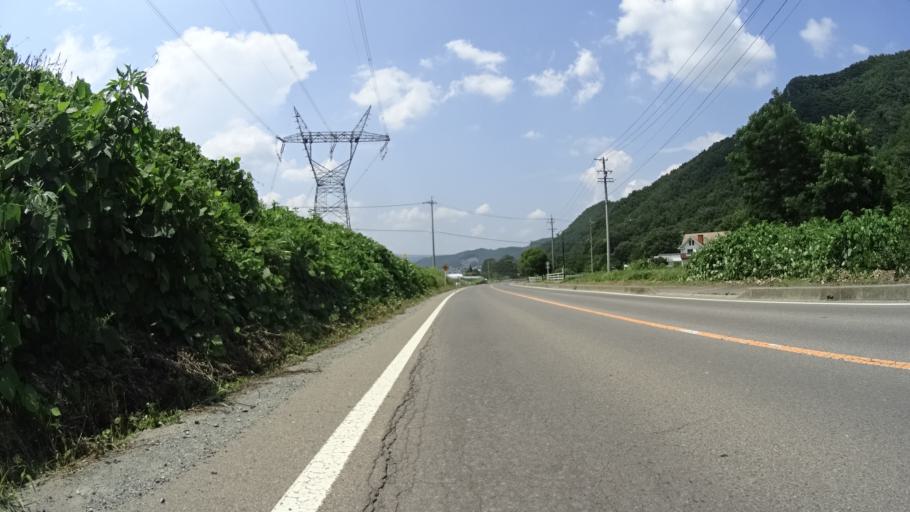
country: JP
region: Nagano
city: Saku
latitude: 36.1434
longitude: 138.5190
